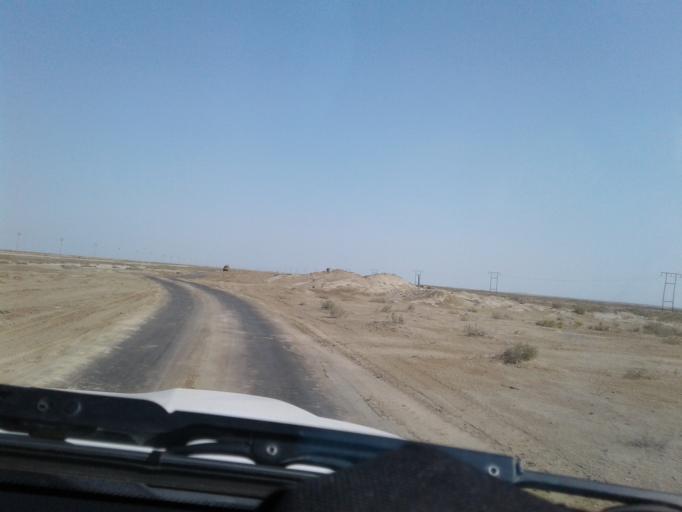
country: IR
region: Golestan
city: Gomishan
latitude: 37.7915
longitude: 53.9181
